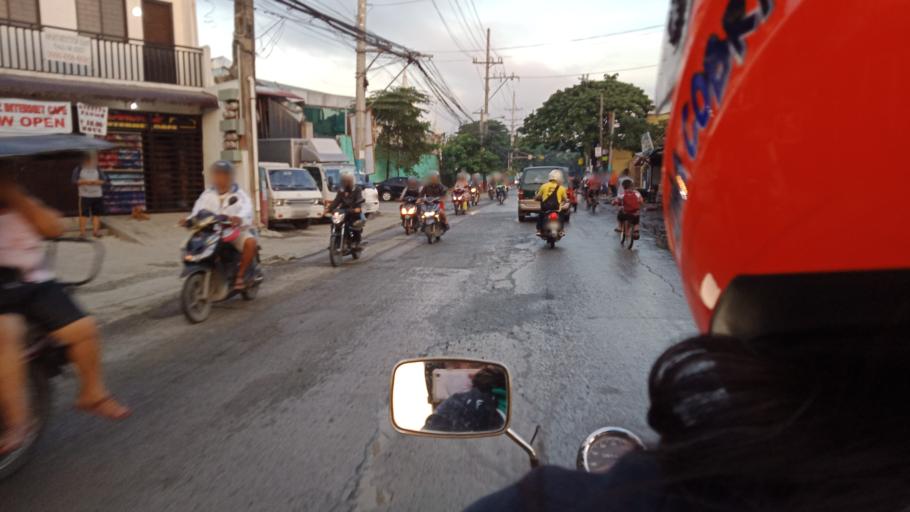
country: PH
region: Calabarzon
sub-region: Province of Rizal
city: Pateros
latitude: 14.5522
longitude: 121.0985
